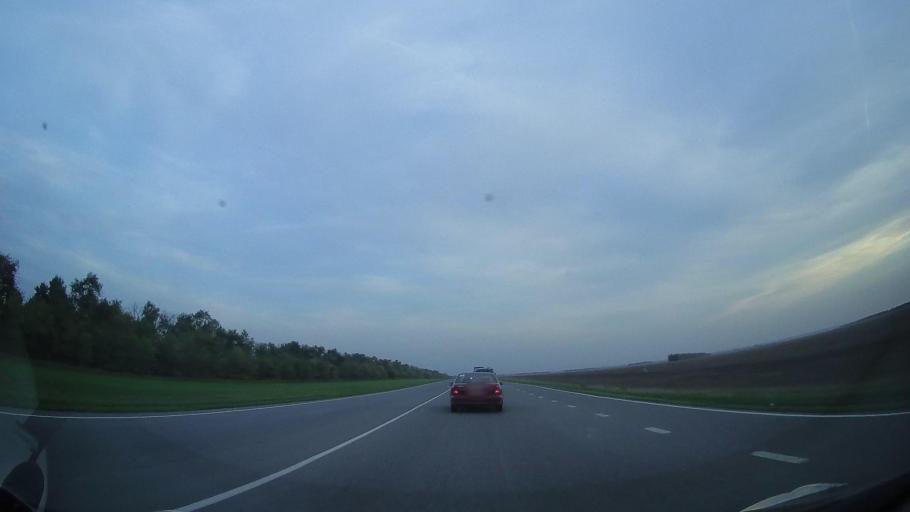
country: RU
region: Rostov
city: Kagal'nitskaya
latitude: 46.9260
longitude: 40.1000
